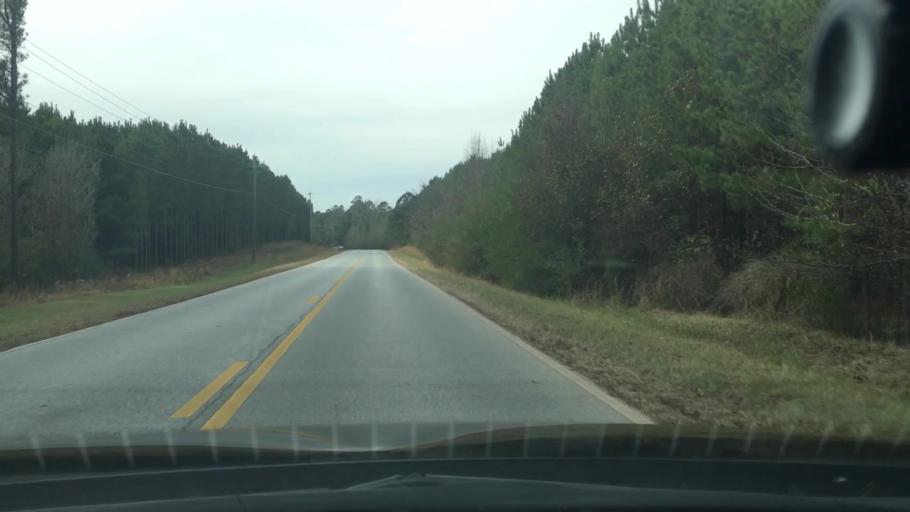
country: US
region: Georgia
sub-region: Spalding County
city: Experiment
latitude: 33.2715
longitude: -84.3489
